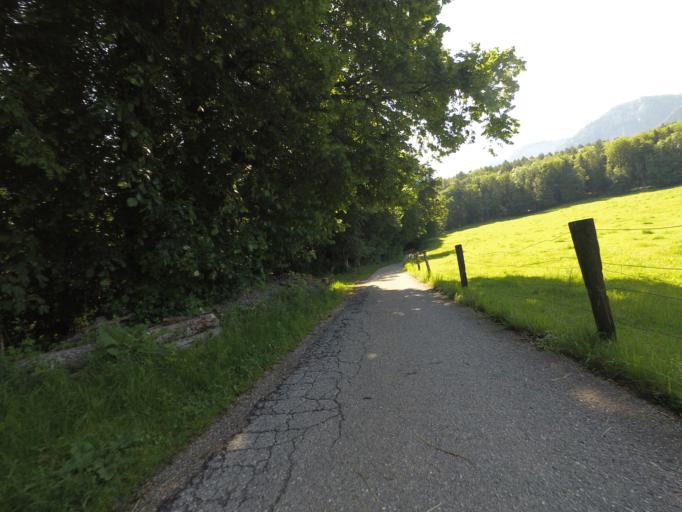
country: DE
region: Bavaria
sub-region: Upper Bavaria
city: Piding
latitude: 47.7374
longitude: 12.9371
